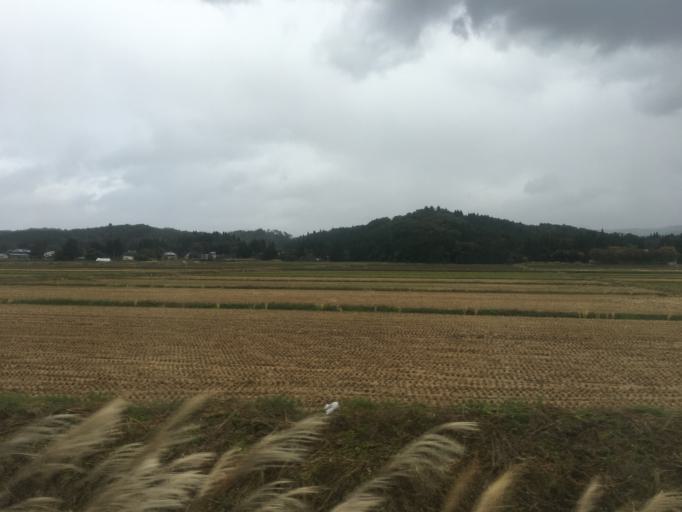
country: JP
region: Yamagata
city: Nagai
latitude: 38.0714
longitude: 139.7371
